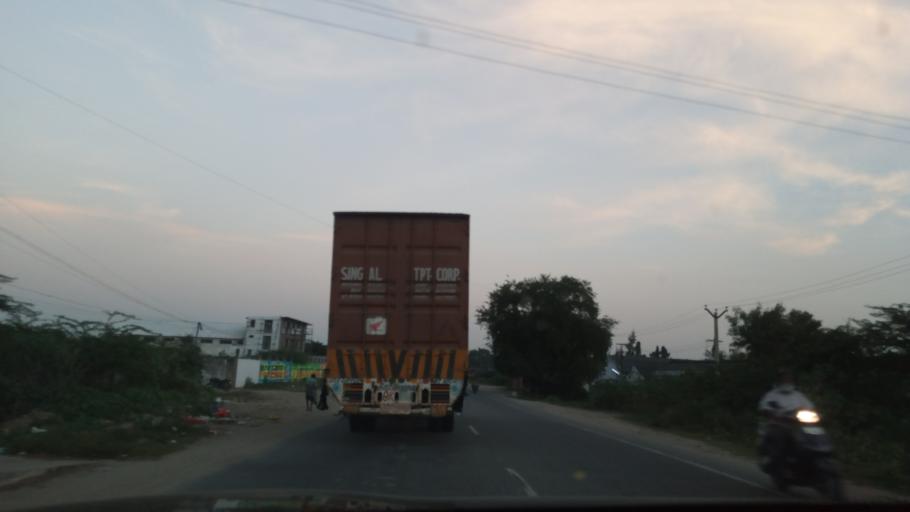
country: IN
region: Tamil Nadu
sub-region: Vellore
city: Walajapet
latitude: 12.9305
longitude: 79.3384
